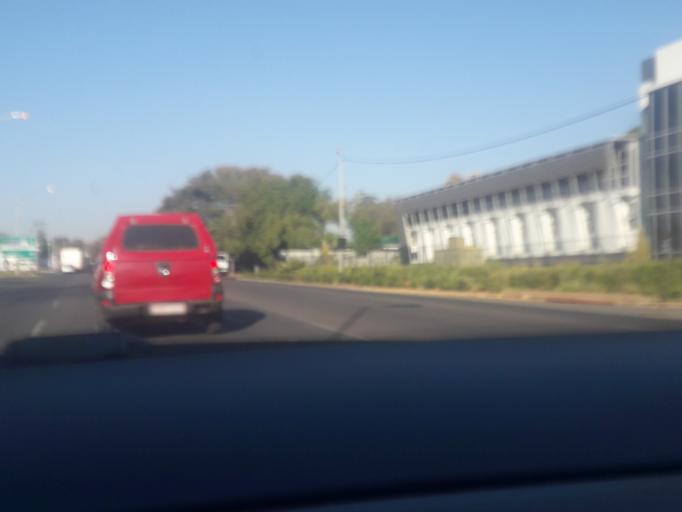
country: ZA
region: Gauteng
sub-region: City of Tshwane Metropolitan Municipality
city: Pretoria
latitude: -25.7619
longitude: 28.2540
